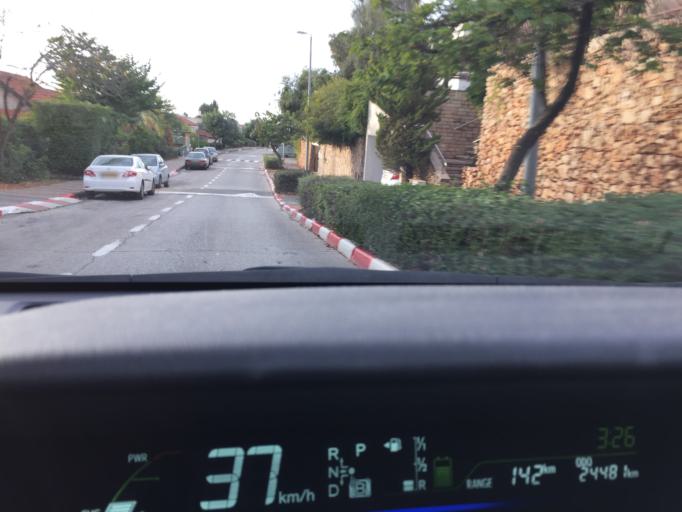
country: PS
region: West Bank
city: Az Zawiyah
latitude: 32.1077
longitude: 35.0358
